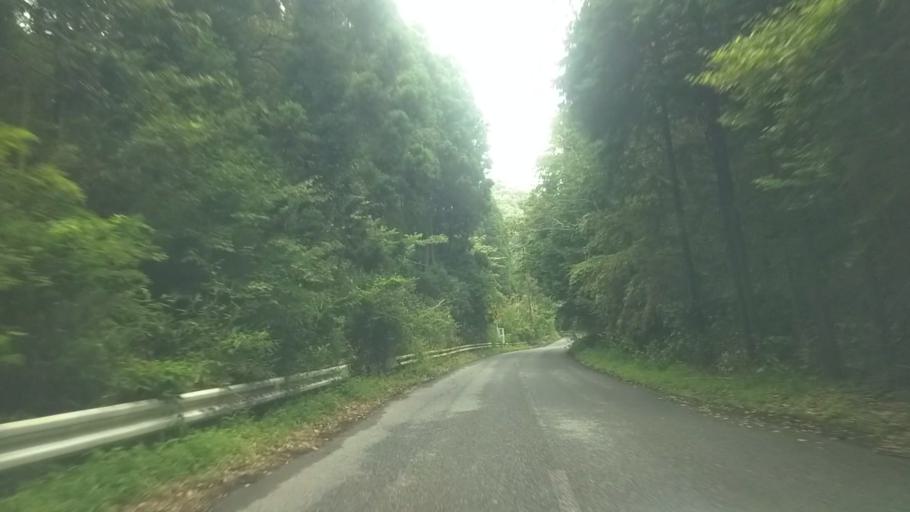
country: JP
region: Chiba
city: Kawaguchi
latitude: 35.2273
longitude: 140.0288
